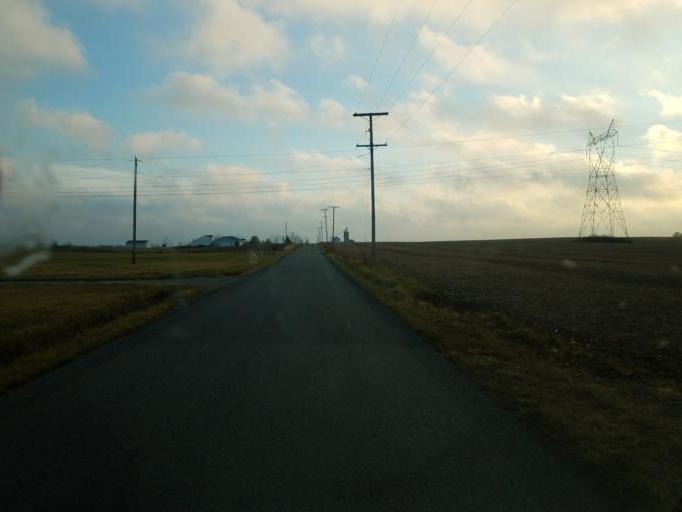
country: US
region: Ohio
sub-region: Knox County
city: Centerburg
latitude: 40.2576
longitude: -82.6407
